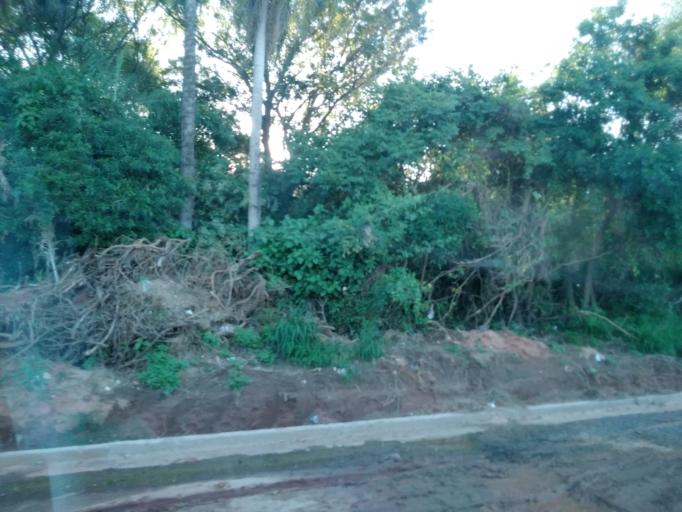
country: AR
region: Corrientes
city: Corrientes
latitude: -27.5072
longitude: -58.7992
